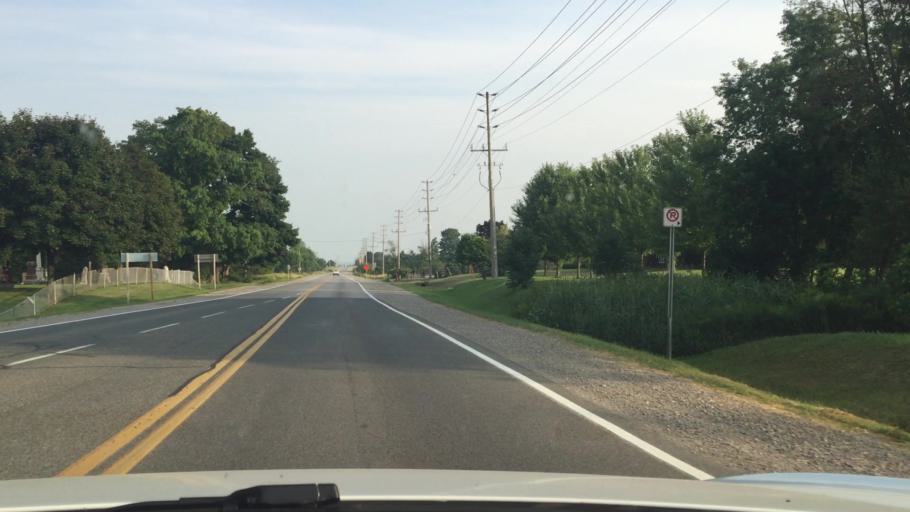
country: CA
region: Ontario
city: Oshawa
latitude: 43.8965
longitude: -78.7715
